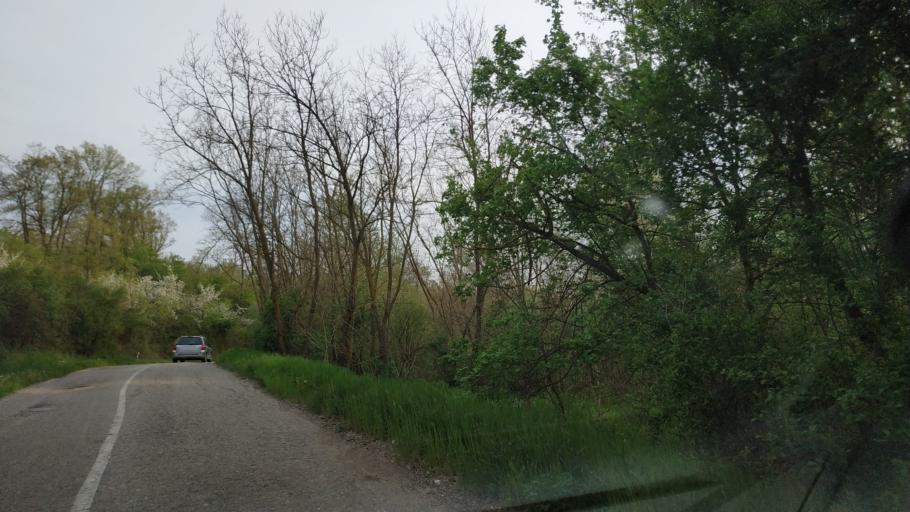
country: RS
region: Central Serbia
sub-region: Nisavski Okrug
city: Aleksinac
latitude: 43.4729
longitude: 21.8104
